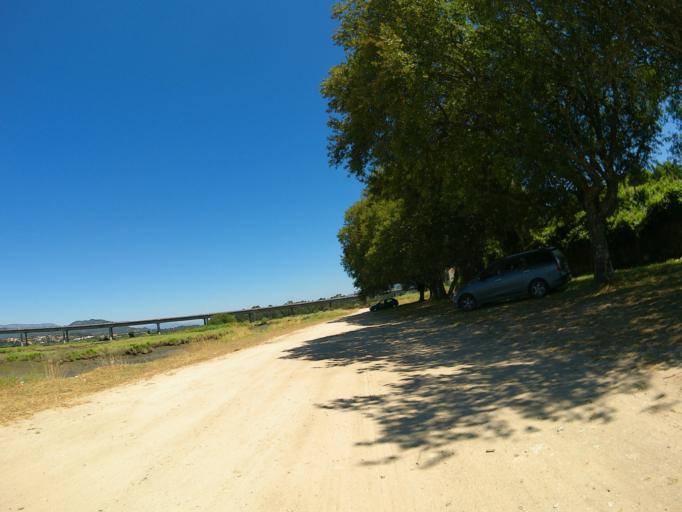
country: PT
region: Viana do Castelo
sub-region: Viana do Castelo
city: Darque
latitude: 41.6877
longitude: -8.7852
